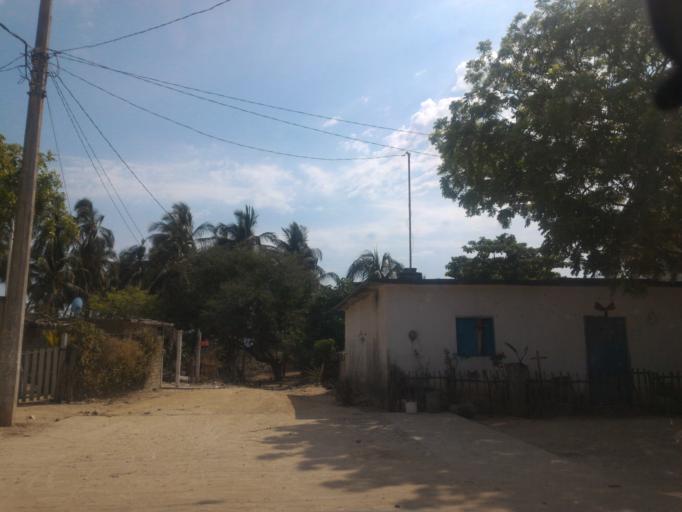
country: MX
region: Michoacan
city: Coahuayana Viejo
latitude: 18.2969
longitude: -103.4101
